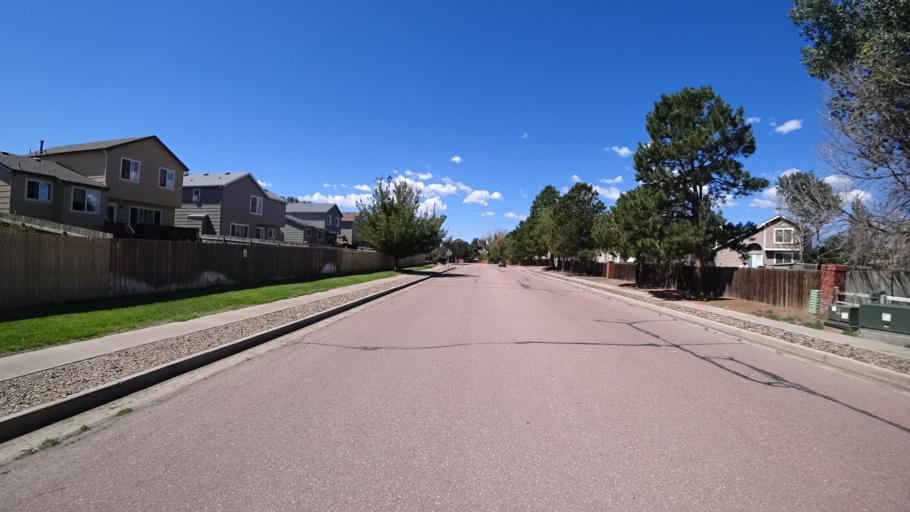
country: US
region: Colorado
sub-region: El Paso County
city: Security-Widefield
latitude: 38.7683
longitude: -104.6533
